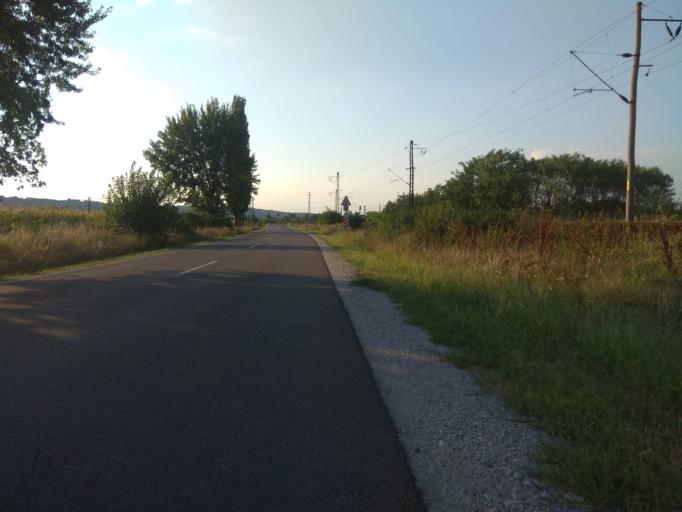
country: HU
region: Borsod-Abauj-Zemplen
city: Nyekladhaza
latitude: 47.9838
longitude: 20.8417
